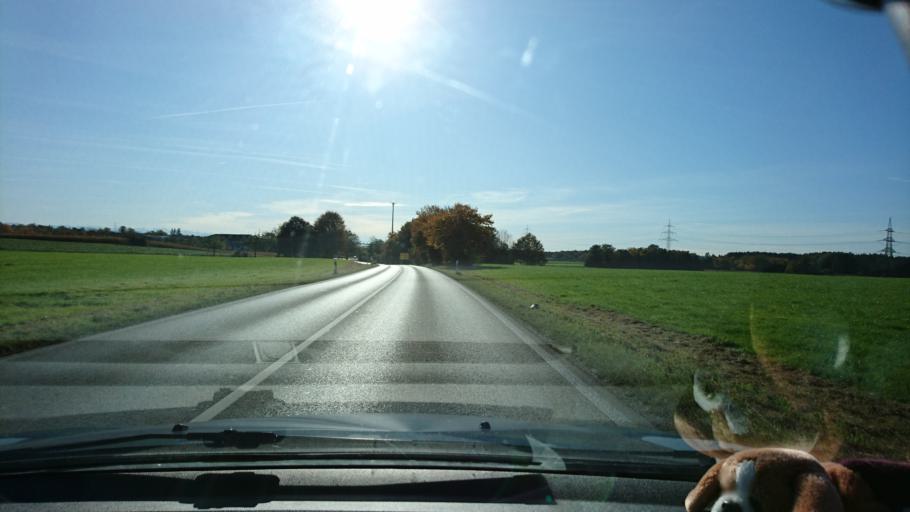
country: DE
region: Bavaria
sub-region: Upper Bavaria
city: Zorneding
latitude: 48.0978
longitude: 11.8251
